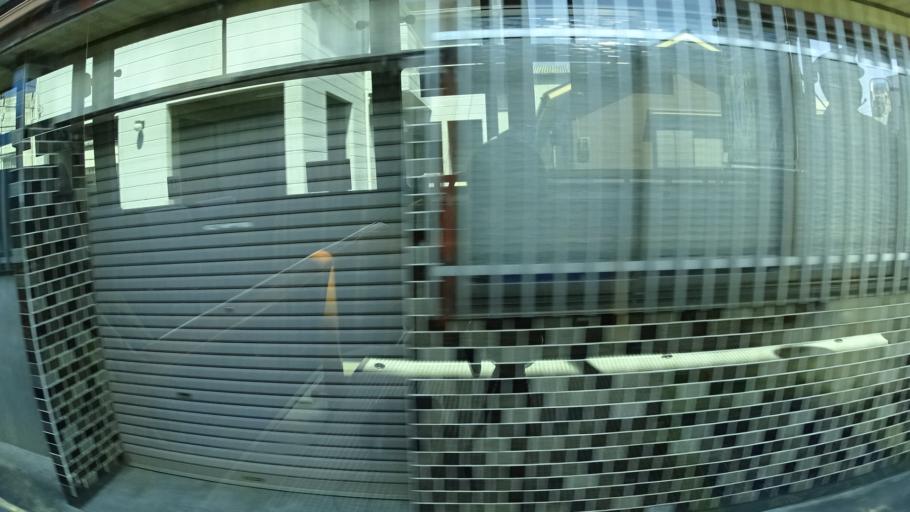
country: JP
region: Mie
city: Toba
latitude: 34.5052
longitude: 136.7773
